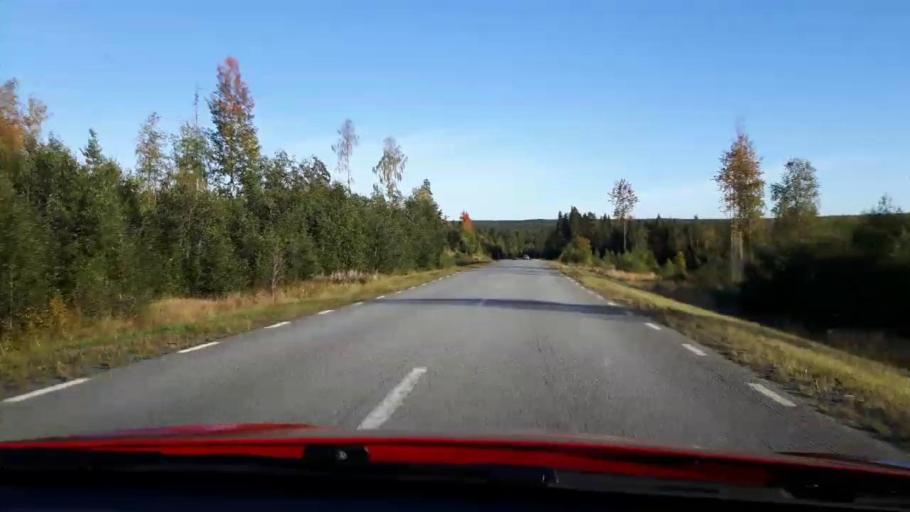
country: SE
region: Jaemtland
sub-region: OEstersunds Kommun
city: Lit
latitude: 63.7451
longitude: 14.7272
